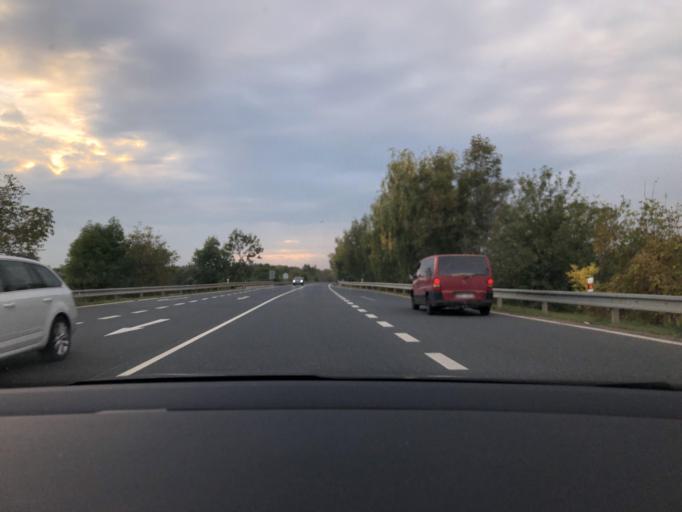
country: CZ
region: Central Bohemia
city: Planany
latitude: 50.0447
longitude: 15.0274
